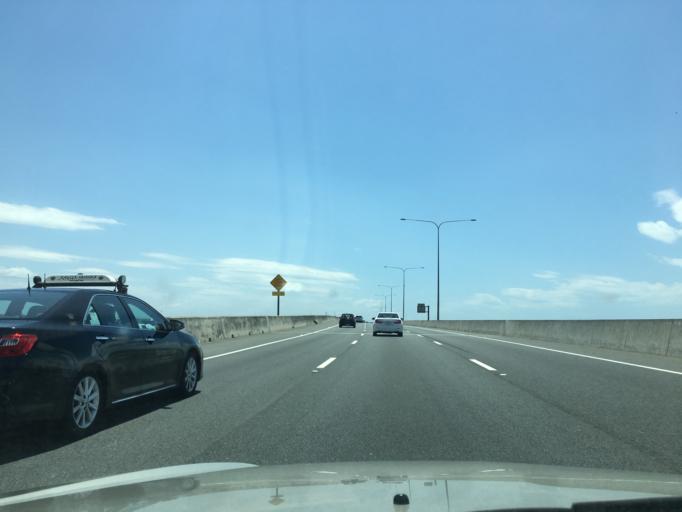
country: AU
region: Queensland
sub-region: Brisbane
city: Wavell Heights
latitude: -27.3985
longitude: 153.0938
